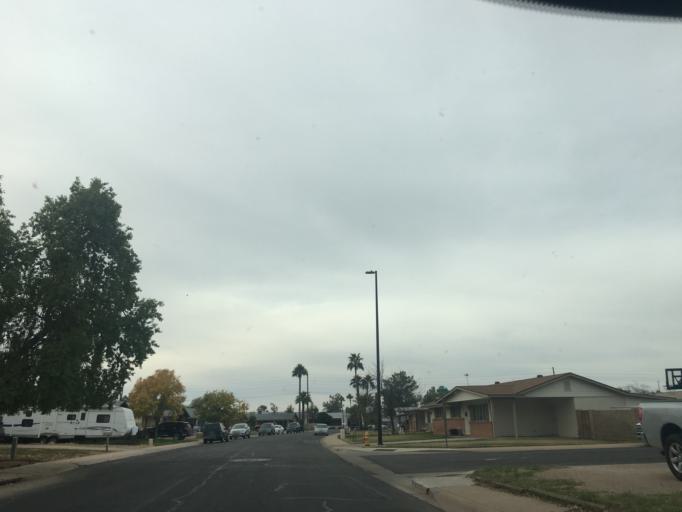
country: US
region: Arizona
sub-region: Maricopa County
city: Gilbert
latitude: 33.3623
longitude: -111.7964
